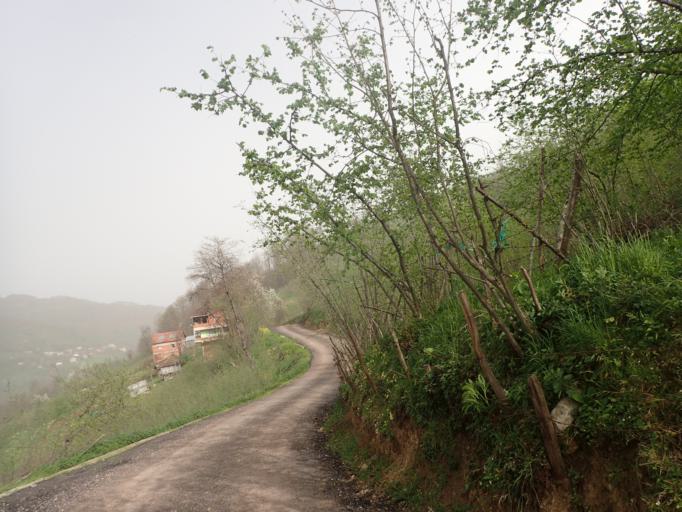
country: TR
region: Ordu
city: Kumru
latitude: 40.8329
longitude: 37.2940
